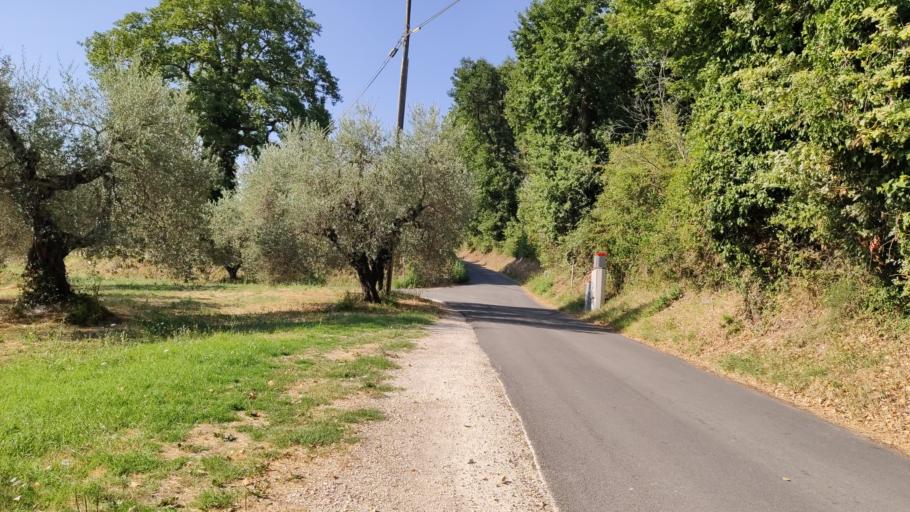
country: IT
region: Umbria
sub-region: Provincia di Terni
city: Amelia
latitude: 42.5403
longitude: 12.4122
